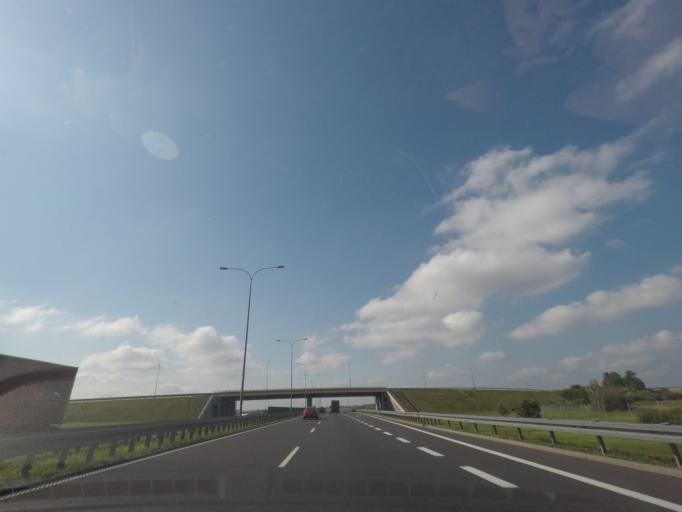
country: PL
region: Pomeranian Voivodeship
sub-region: Powiat starogardzki
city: Smetowo Graniczne
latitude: 53.7375
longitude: 18.6298
